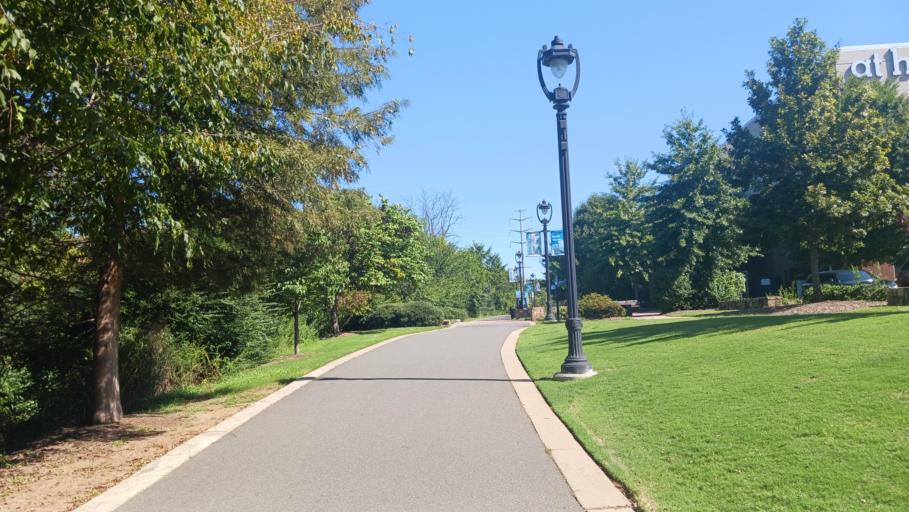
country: US
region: North Carolina
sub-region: Mecklenburg County
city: Charlotte
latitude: 35.2143
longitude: -80.8358
